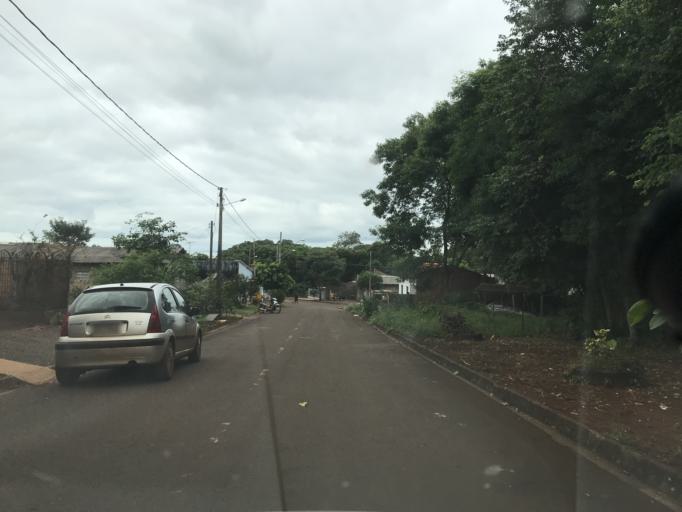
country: BR
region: Parana
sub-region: Palotina
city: Palotina
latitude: -24.3002
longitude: -53.8297
